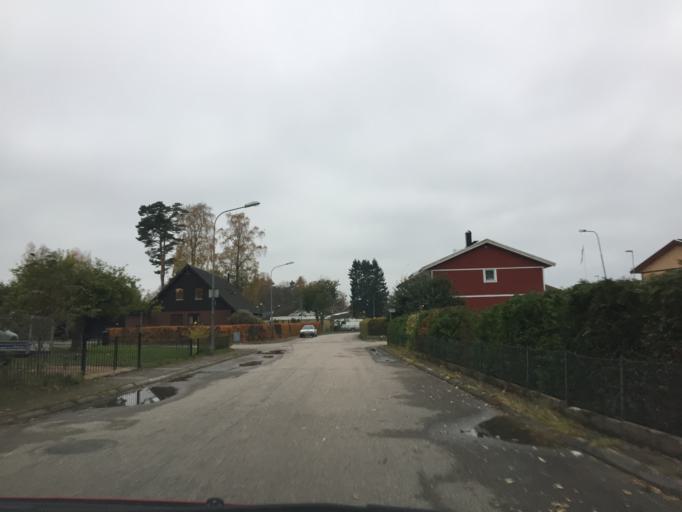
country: SE
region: Vaestra Goetaland
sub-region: Trollhattan
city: Trollhattan
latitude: 58.2579
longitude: 12.2882
